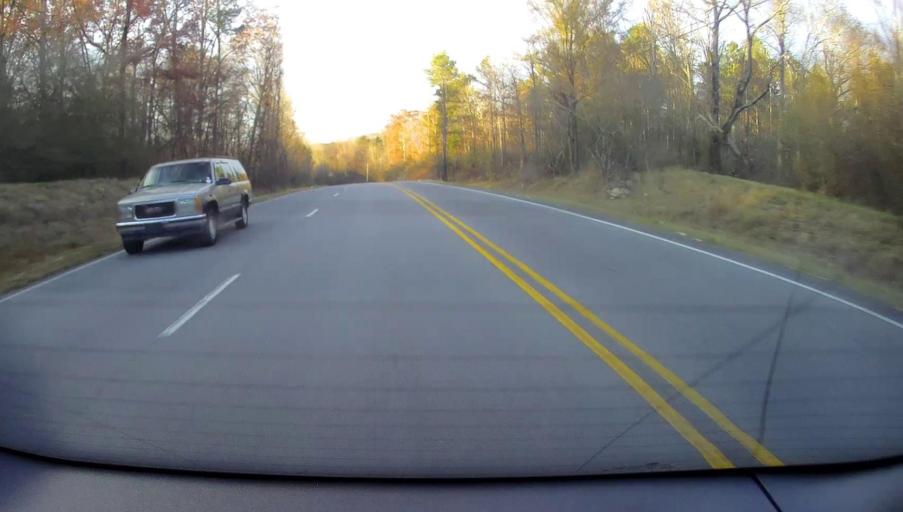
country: US
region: Alabama
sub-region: Blount County
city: Blountsville
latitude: 34.1493
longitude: -86.4525
